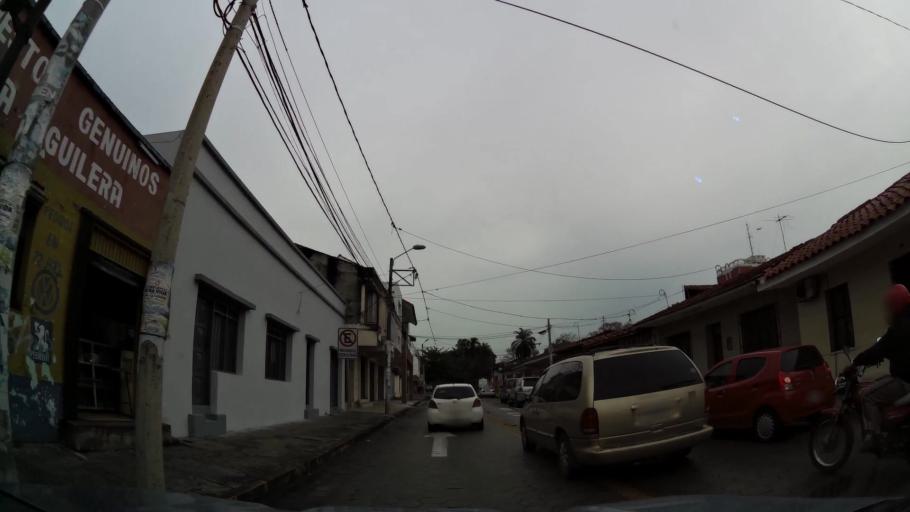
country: BO
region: Santa Cruz
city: Santa Cruz de la Sierra
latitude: -17.7897
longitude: -63.1842
